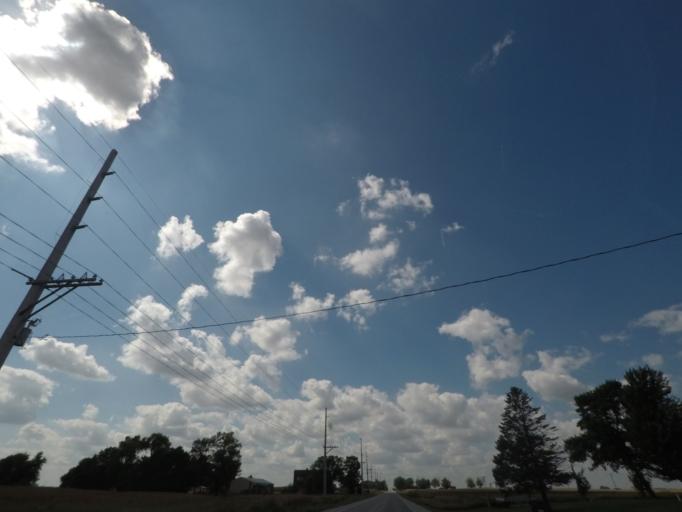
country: US
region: Iowa
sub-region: Story County
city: Ames
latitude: 42.0231
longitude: -93.5379
